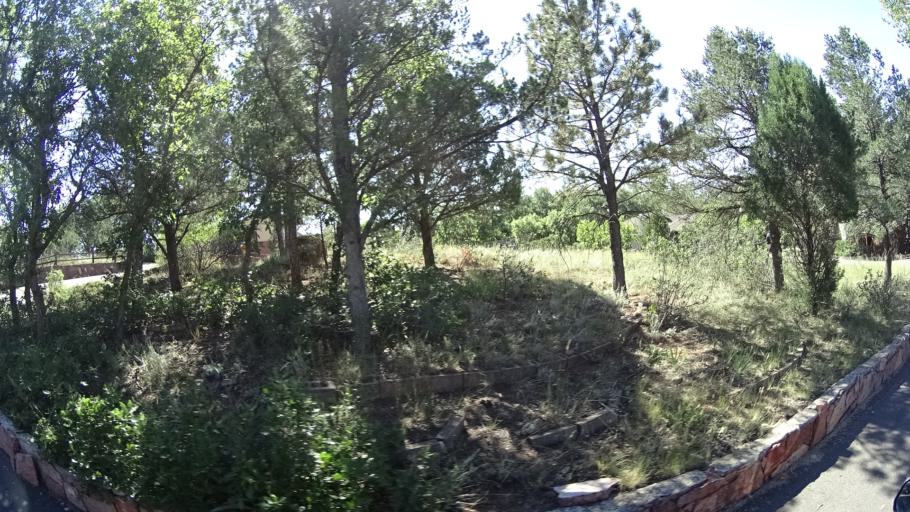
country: US
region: Colorado
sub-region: El Paso County
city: Manitou Springs
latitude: 38.8674
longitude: -104.8831
